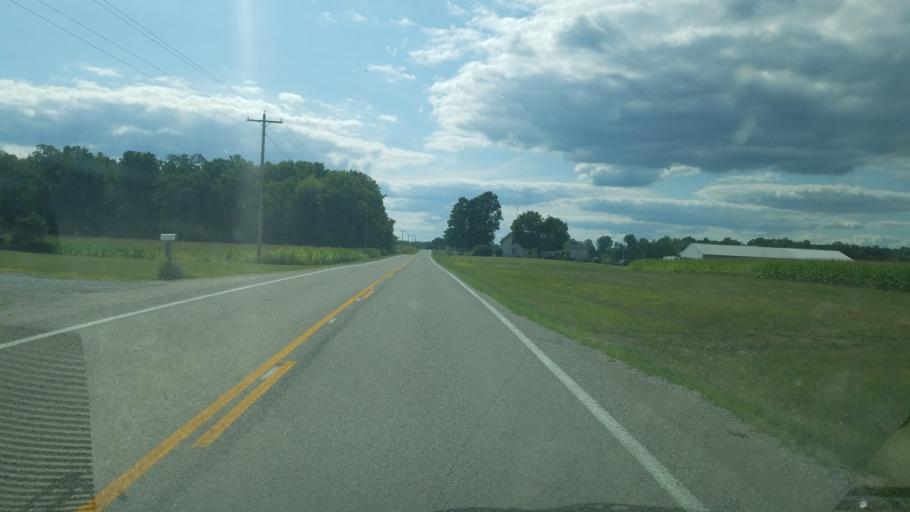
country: US
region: Ohio
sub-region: Logan County
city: De Graff
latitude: 40.2447
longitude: -83.9315
